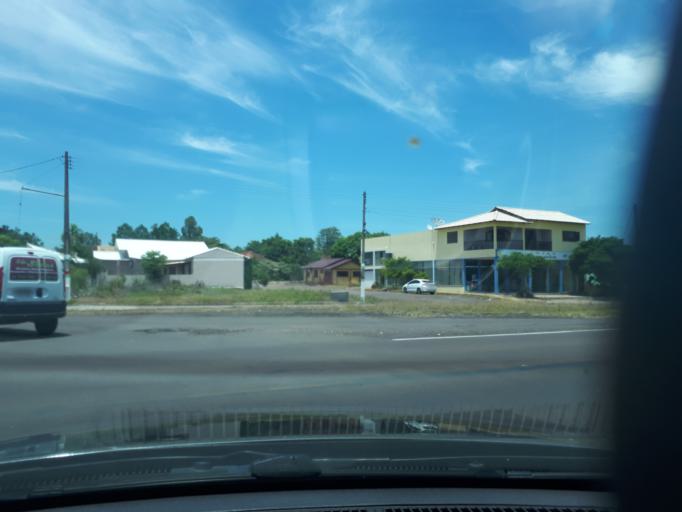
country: BR
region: Rio Grande do Sul
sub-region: Candelaria
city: Candelaria
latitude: -29.7325
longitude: -52.9474
